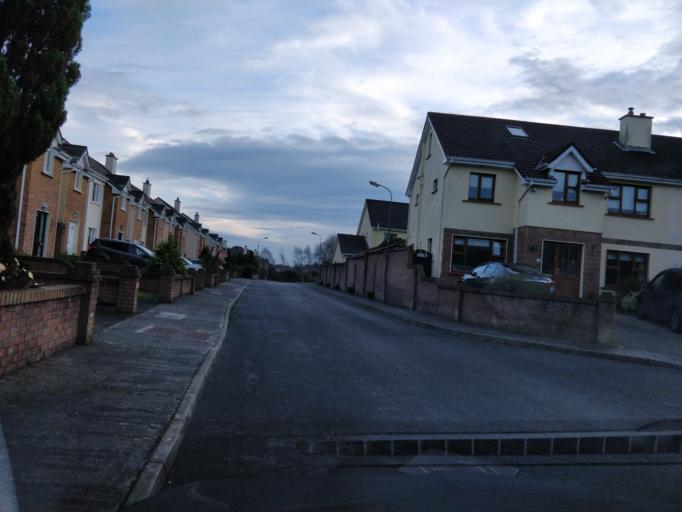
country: IE
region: Connaught
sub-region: County Galway
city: Bearna
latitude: 53.2686
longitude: -9.1090
